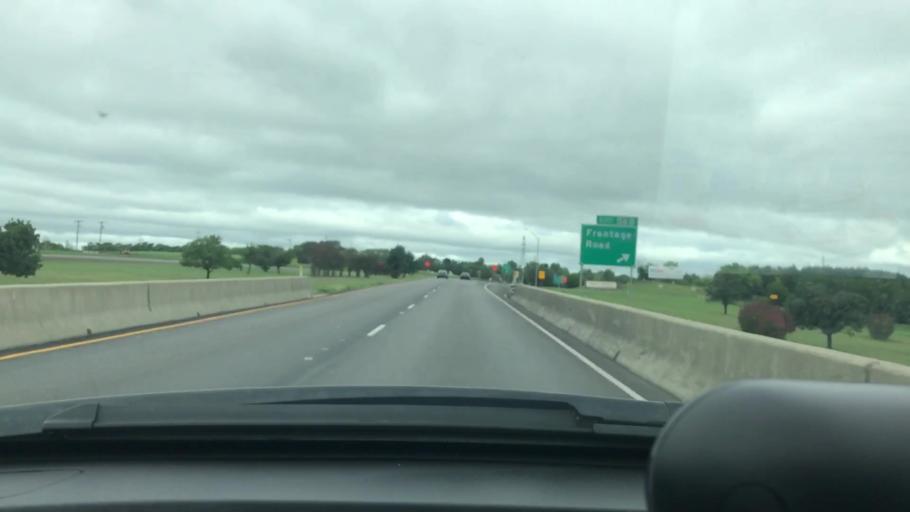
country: US
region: Texas
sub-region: Grayson County
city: Sherman
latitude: 33.6009
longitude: -96.6075
